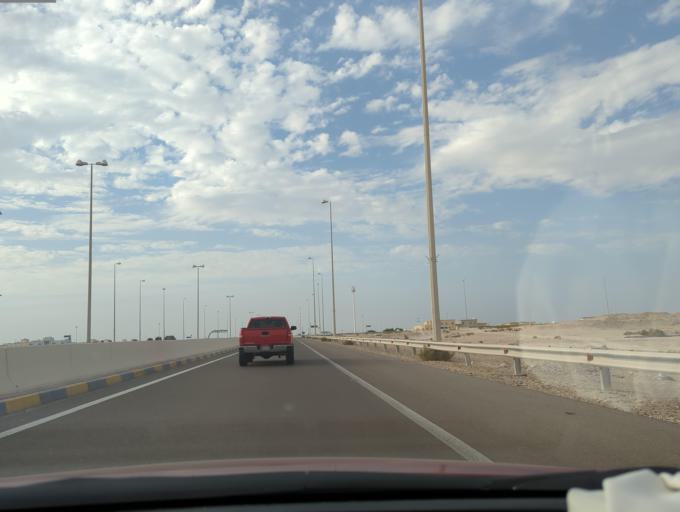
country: AE
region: Abu Dhabi
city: Abu Dhabi
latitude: 24.3999
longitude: 54.7527
